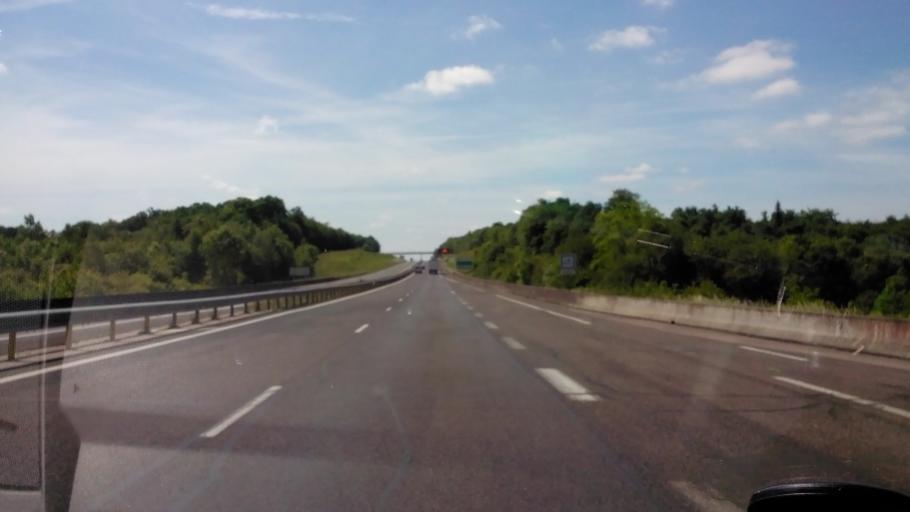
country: FR
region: Lorraine
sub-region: Departement de Meurthe-et-Moselle
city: Dommartin-les-Toul
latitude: 48.6470
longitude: 5.8801
